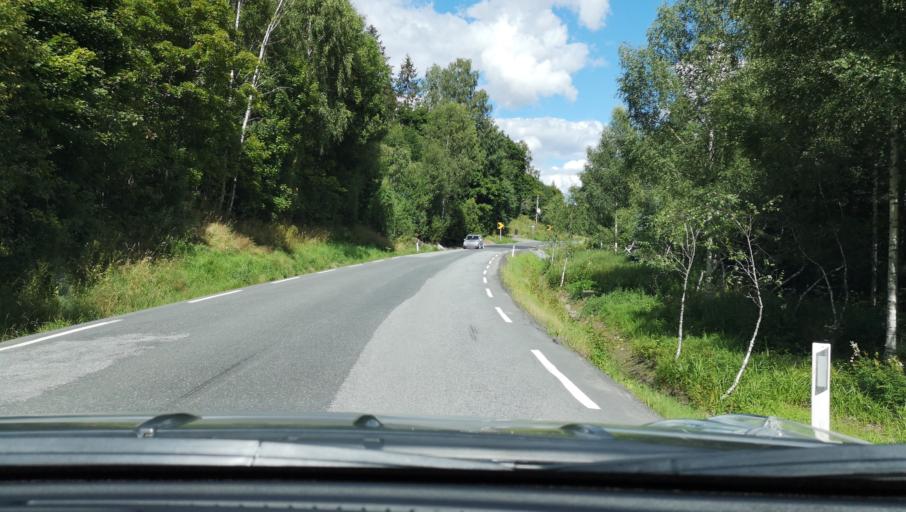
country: NO
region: Ostfold
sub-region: Hobol
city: Elvestad
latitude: 59.6402
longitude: 10.9670
